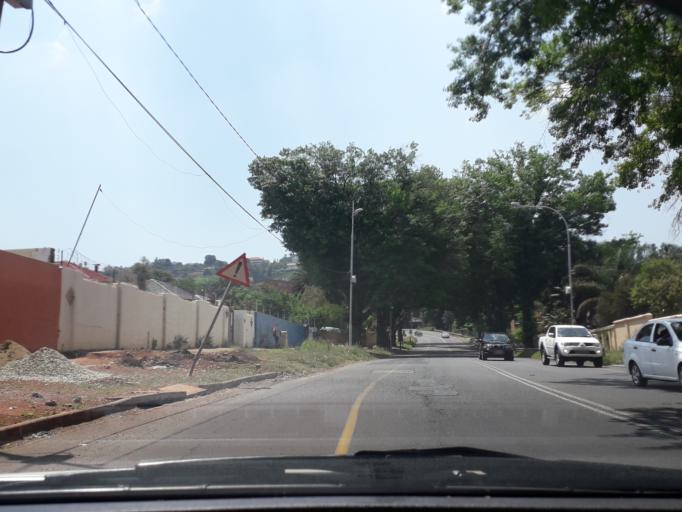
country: ZA
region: Gauteng
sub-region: City of Johannesburg Metropolitan Municipality
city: Johannesburg
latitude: -26.1745
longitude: 28.1010
